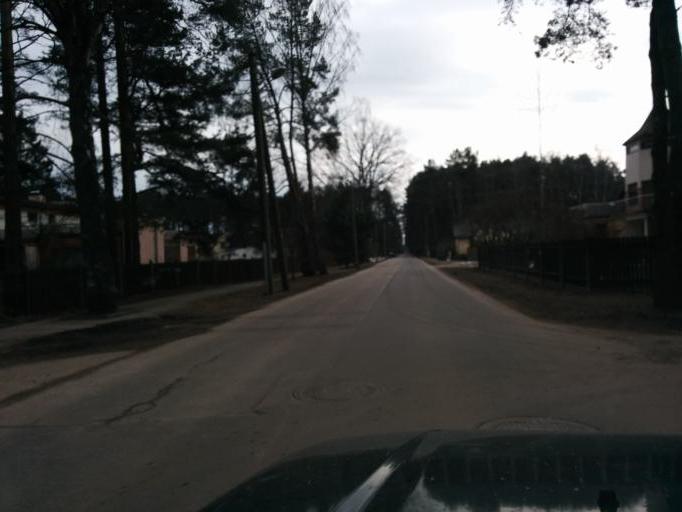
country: LV
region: Jurmala
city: Jurmala
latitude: 56.9522
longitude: 23.7248
